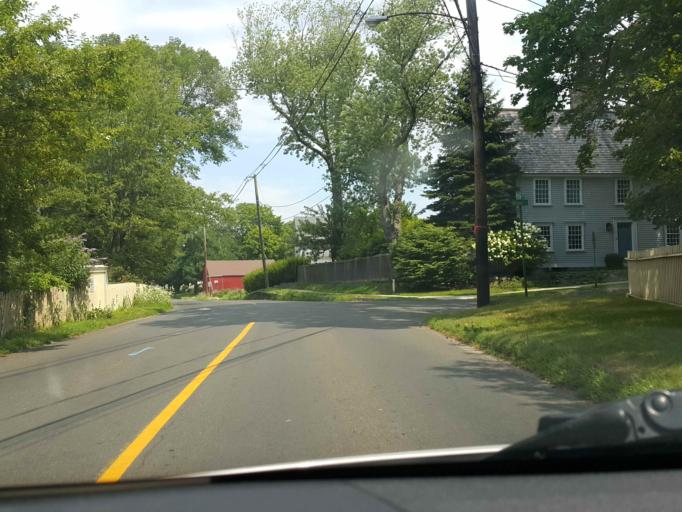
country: US
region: Connecticut
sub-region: New Haven County
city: Guilford
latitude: 41.2837
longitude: -72.6872
